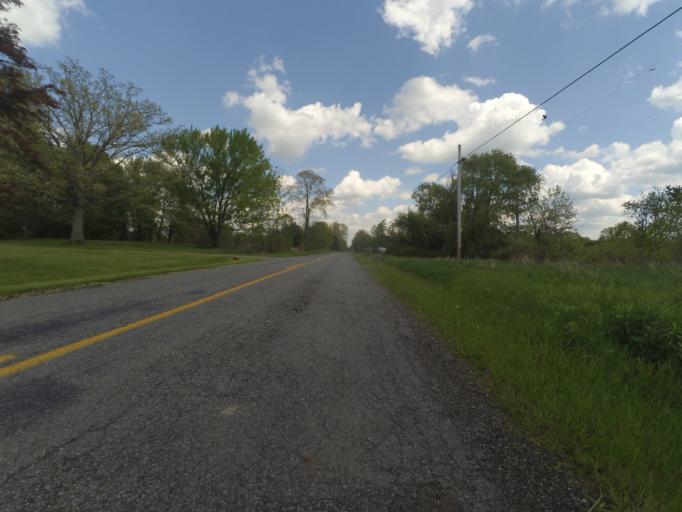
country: US
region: Ohio
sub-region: Mahoning County
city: Craig Beach
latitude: 41.1341
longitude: -81.0165
